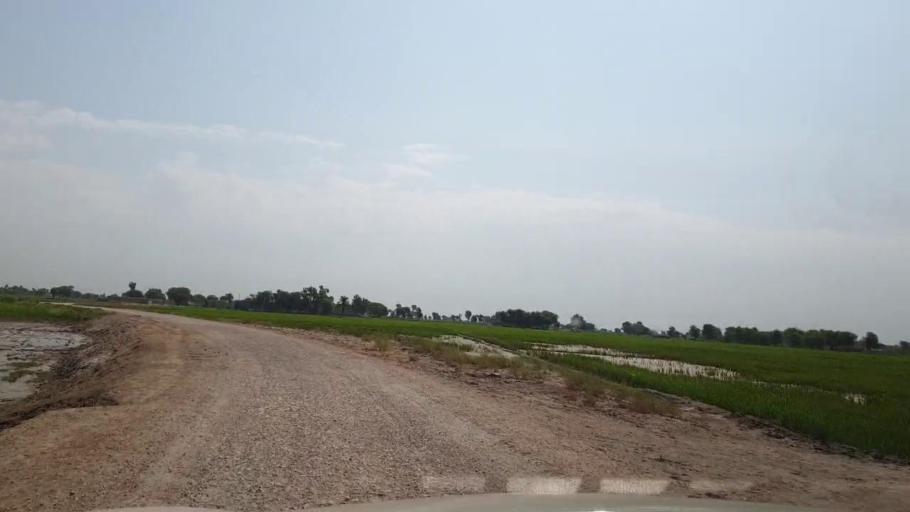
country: PK
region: Sindh
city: Ratodero
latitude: 27.8348
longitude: 68.2822
